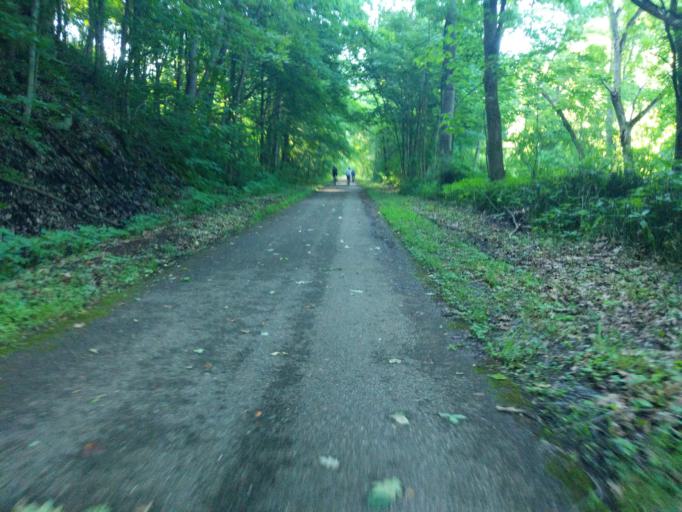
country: US
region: Ohio
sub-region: Athens County
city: Nelsonville
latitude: 39.4211
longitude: -82.1954
